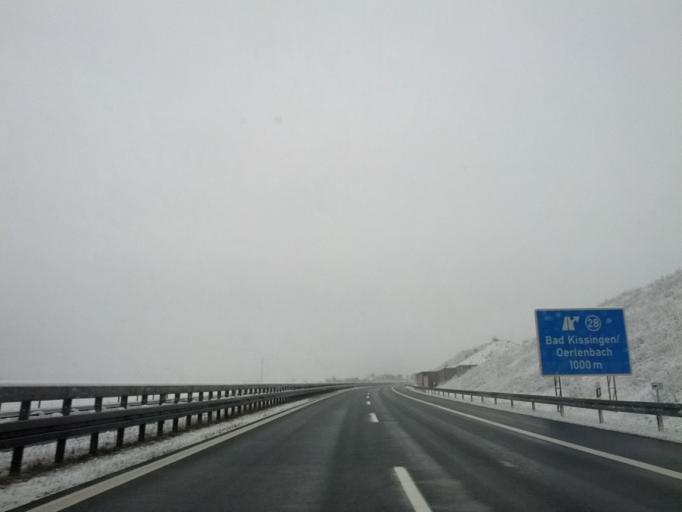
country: DE
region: Bavaria
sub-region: Regierungsbezirk Unterfranken
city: Oerlenbach
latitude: 50.1303
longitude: 10.1499
